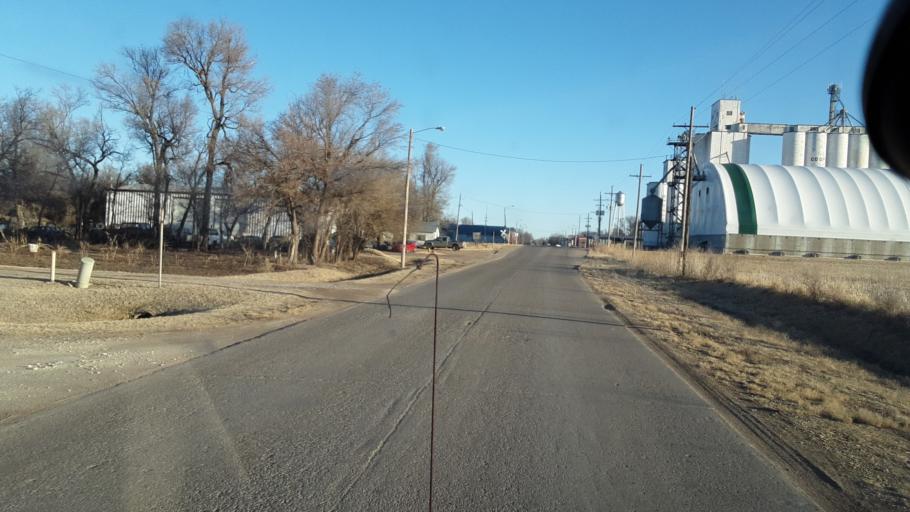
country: US
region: Kansas
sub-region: Rice County
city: Lyons
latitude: 38.3505
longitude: -98.3495
